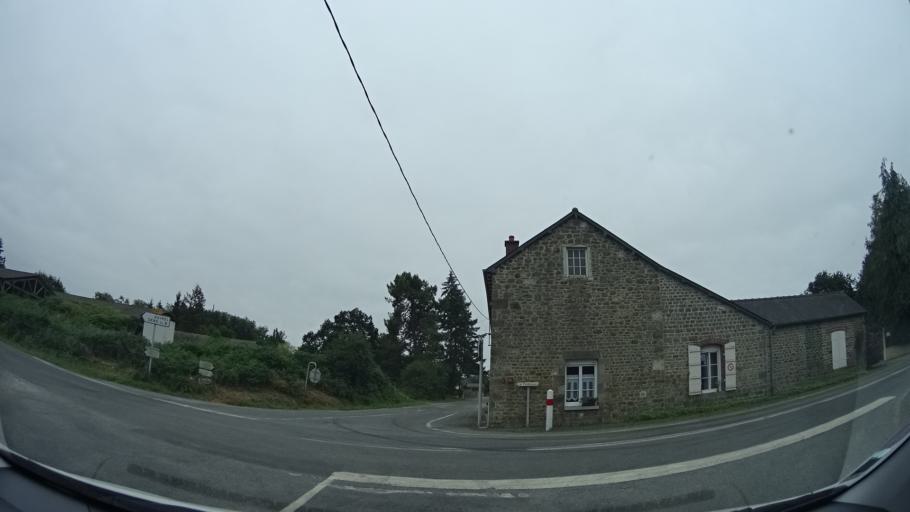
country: FR
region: Brittany
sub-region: Departement d'Ille-et-Vilaine
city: Hede-Bazouges
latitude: 48.2988
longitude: -1.7675
